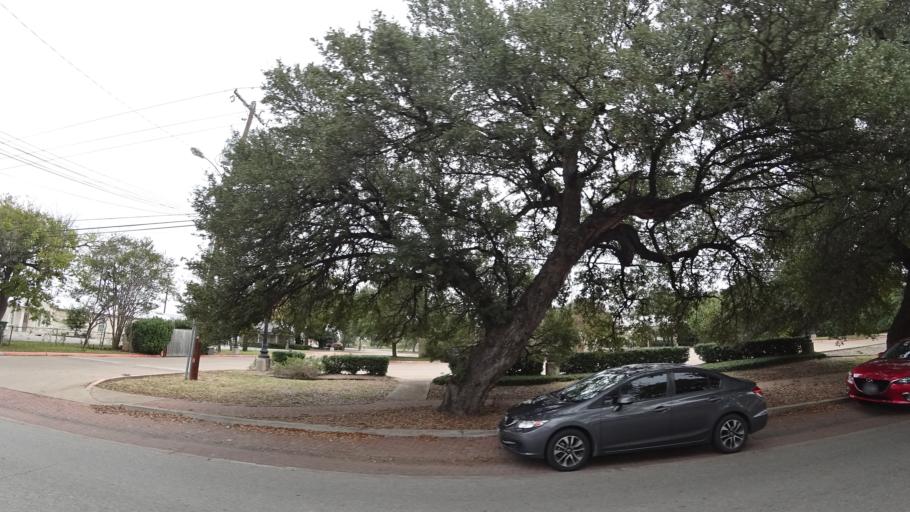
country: US
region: Texas
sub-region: Williamson County
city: Round Rock
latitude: 30.5154
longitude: -97.6900
